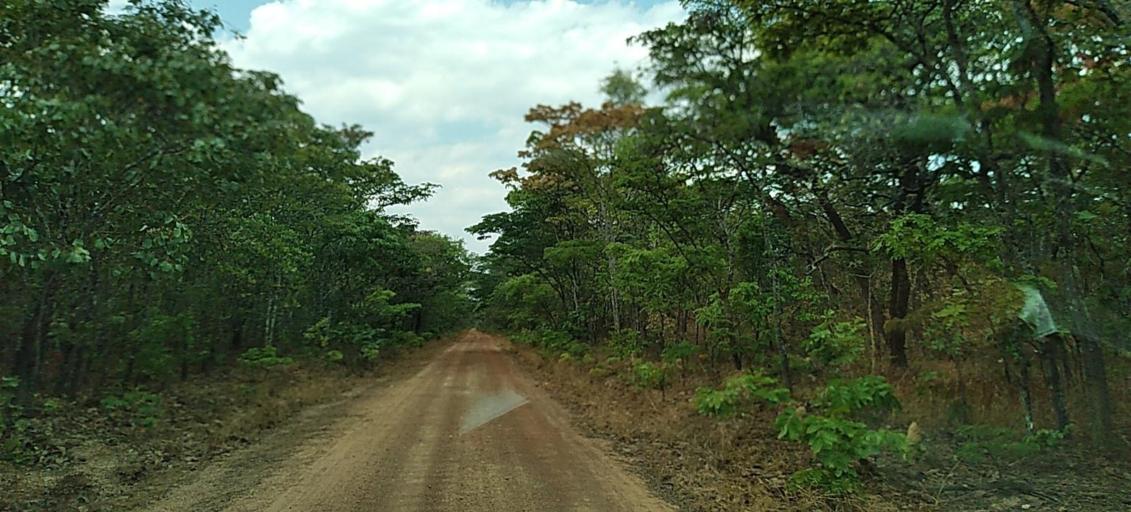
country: ZM
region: Copperbelt
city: Chililabombwe
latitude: -12.4589
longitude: 27.5991
